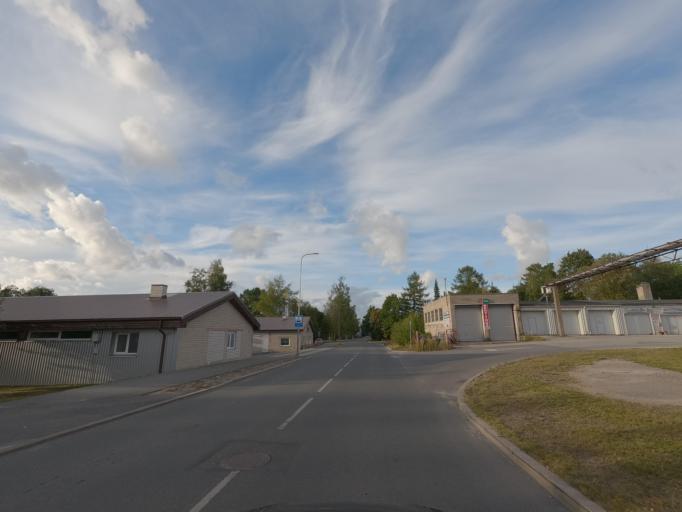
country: EE
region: Raplamaa
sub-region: Rapla vald
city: Rapla
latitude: 58.9967
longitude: 24.7986
